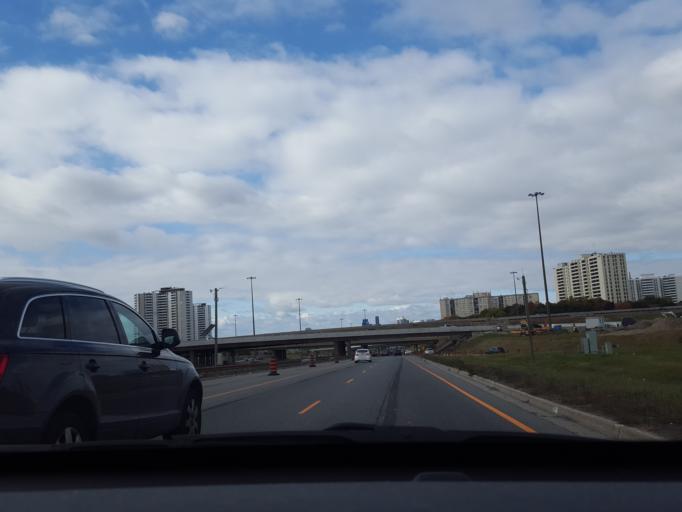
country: CA
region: Ontario
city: Willowdale
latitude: 43.7684
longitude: -79.3345
